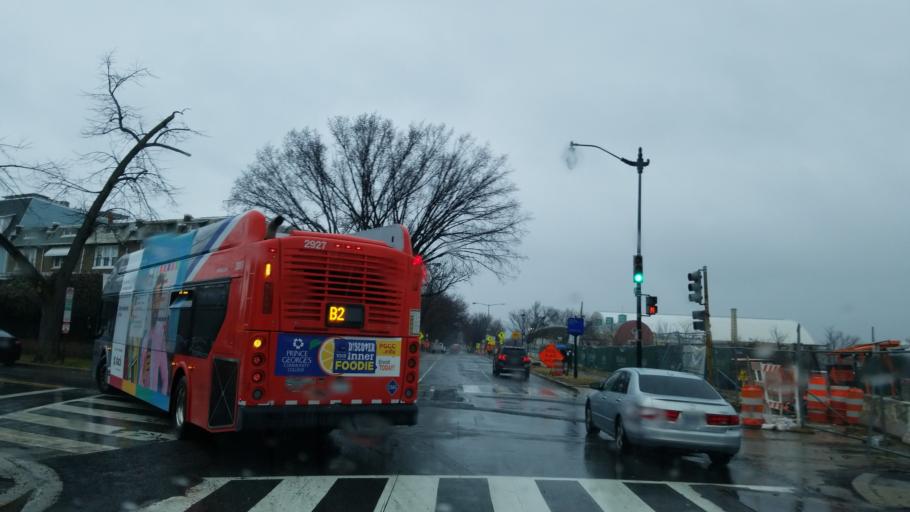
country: US
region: Maryland
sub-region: Prince George's County
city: Silver Hill
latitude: 38.8844
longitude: -76.9772
